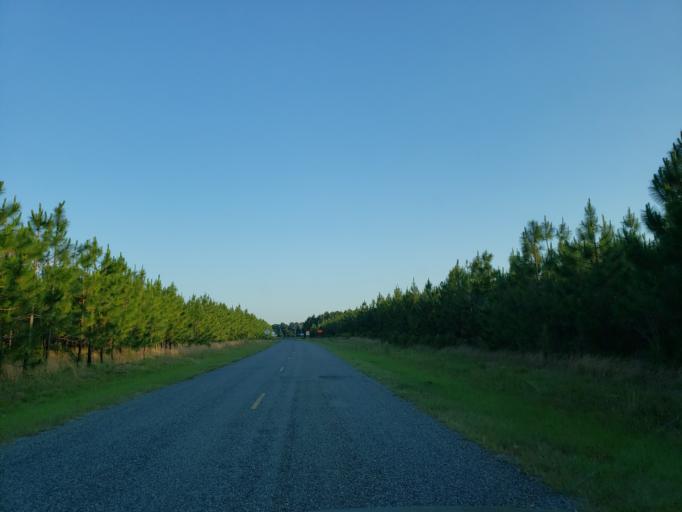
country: US
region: Georgia
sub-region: Dooly County
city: Vienna
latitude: 32.1101
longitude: -83.7557
